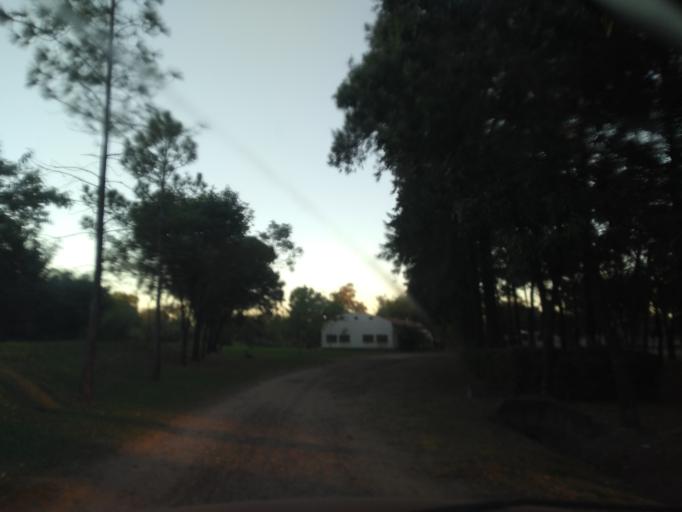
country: AR
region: Chaco
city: Fontana
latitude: -27.4242
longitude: -59.0043
